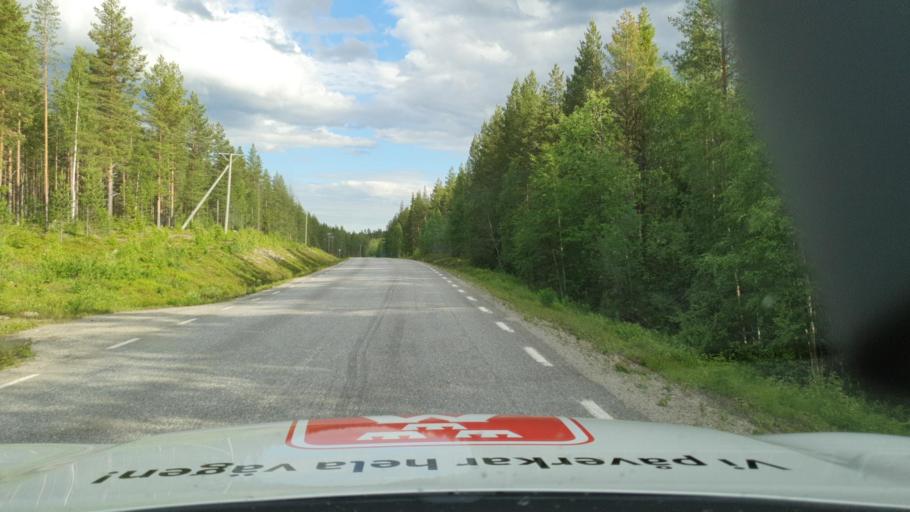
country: SE
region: Vaesterbotten
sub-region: Vindelns Kommun
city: Vindeln
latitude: 64.3952
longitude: 19.6705
